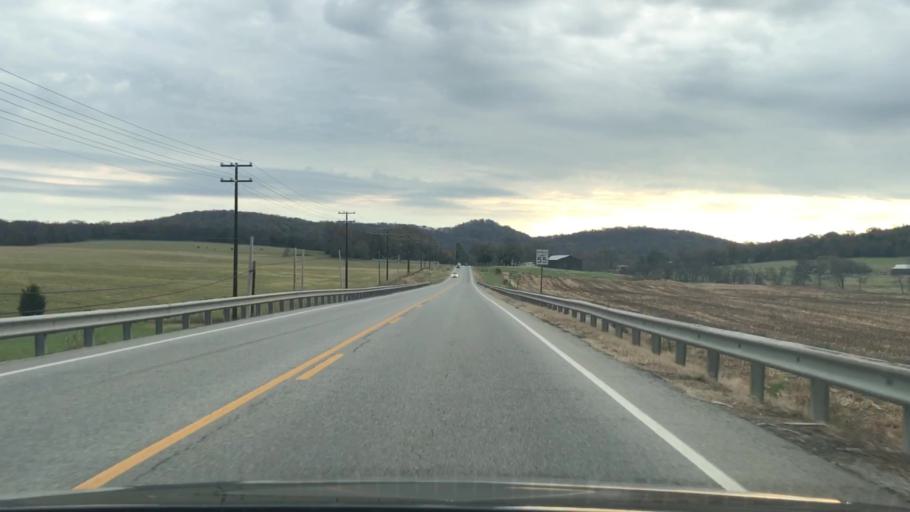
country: US
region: Tennessee
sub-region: Trousdale County
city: Hartsville
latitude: 36.3850
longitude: -86.1278
